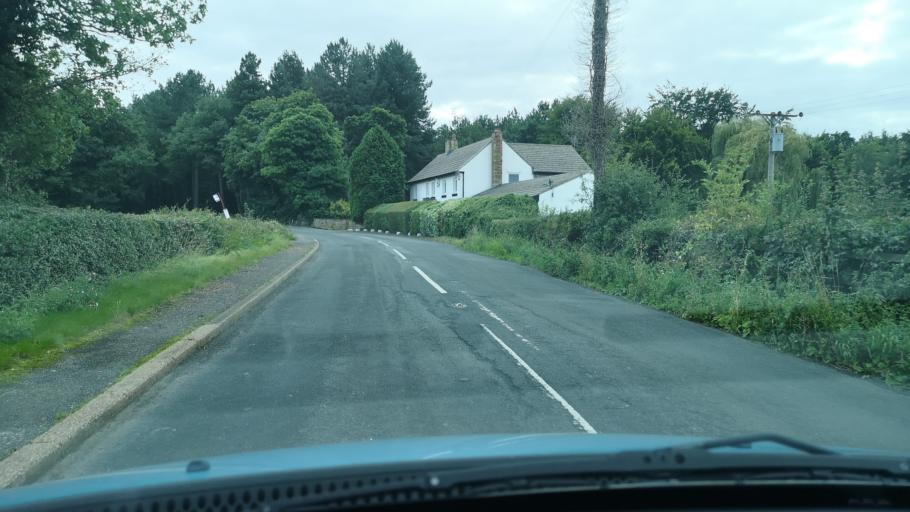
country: GB
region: England
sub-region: City and Borough of Wakefield
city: Crigglestone
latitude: 53.6309
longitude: -1.5517
